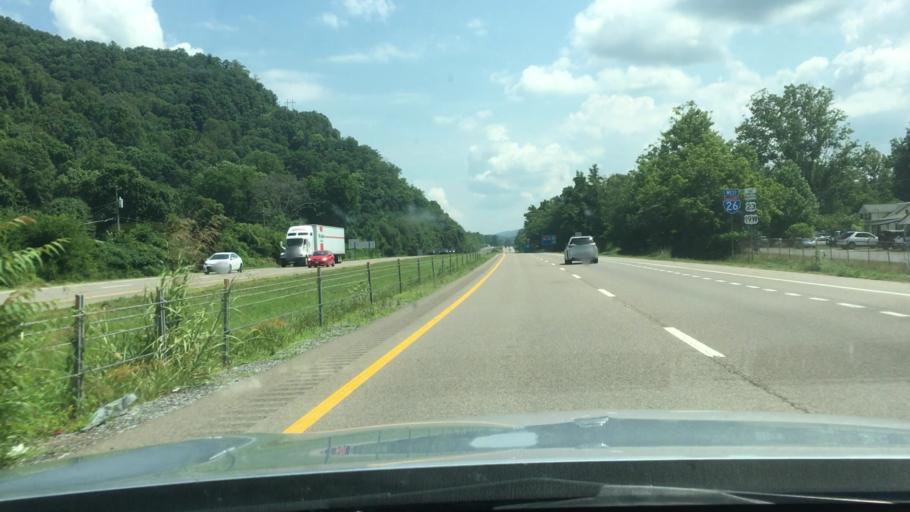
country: US
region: Tennessee
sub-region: Unicoi County
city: Erwin
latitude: 36.1539
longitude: -82.4153
